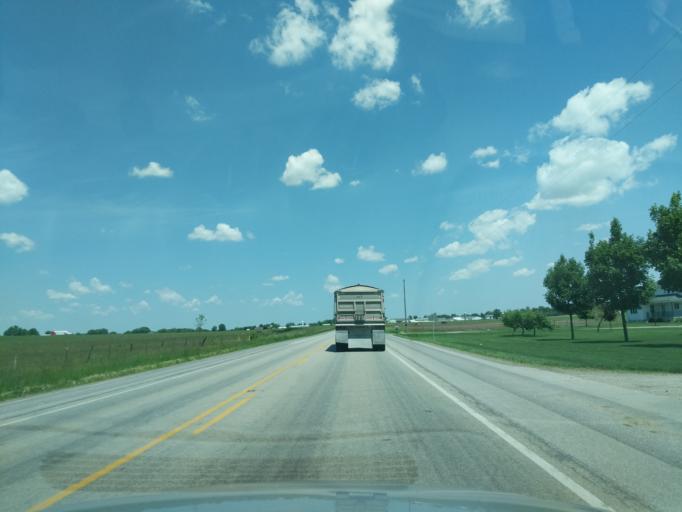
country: US
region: Indiana
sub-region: LaGrange County
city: Topeka
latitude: 41.6388
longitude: -85.5799
